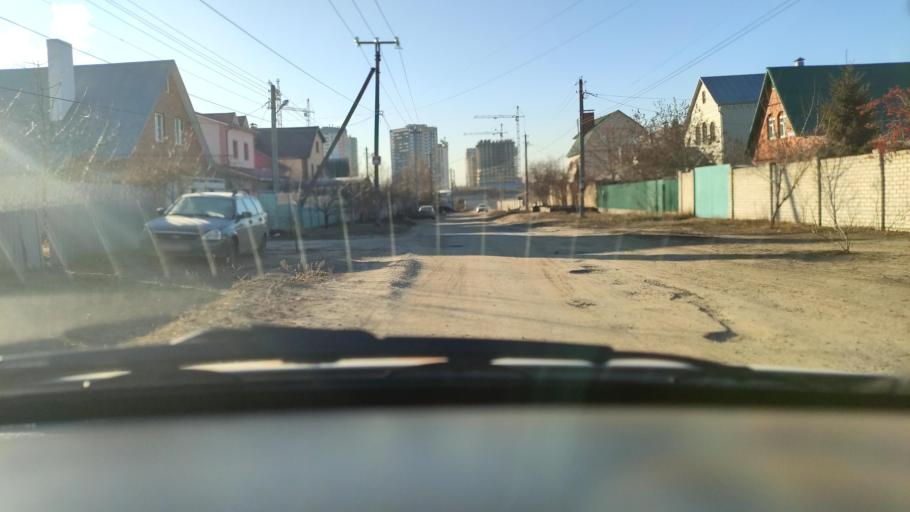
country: RU
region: Voronezj
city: Podgornoye
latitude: 51.7228
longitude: 39.1502
